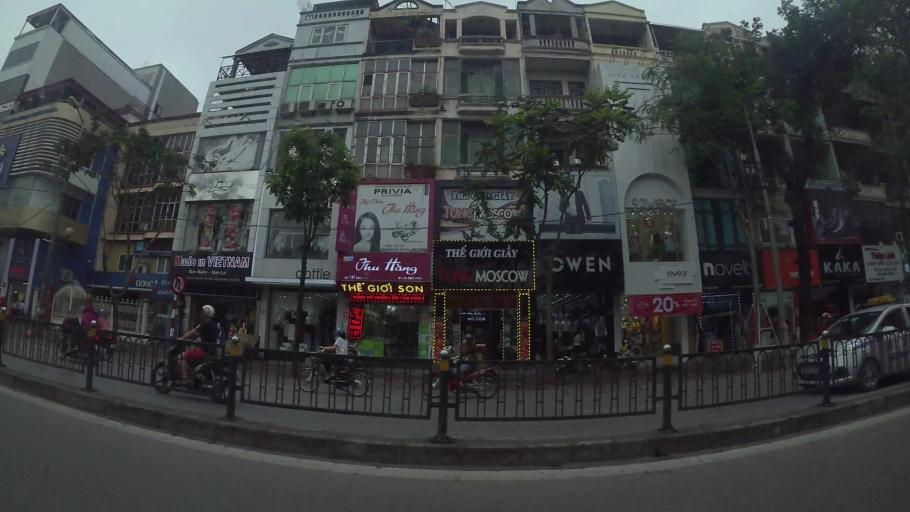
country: VN
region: Ha Noi
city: Dong Da
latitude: 21.0079
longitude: 105.8282
